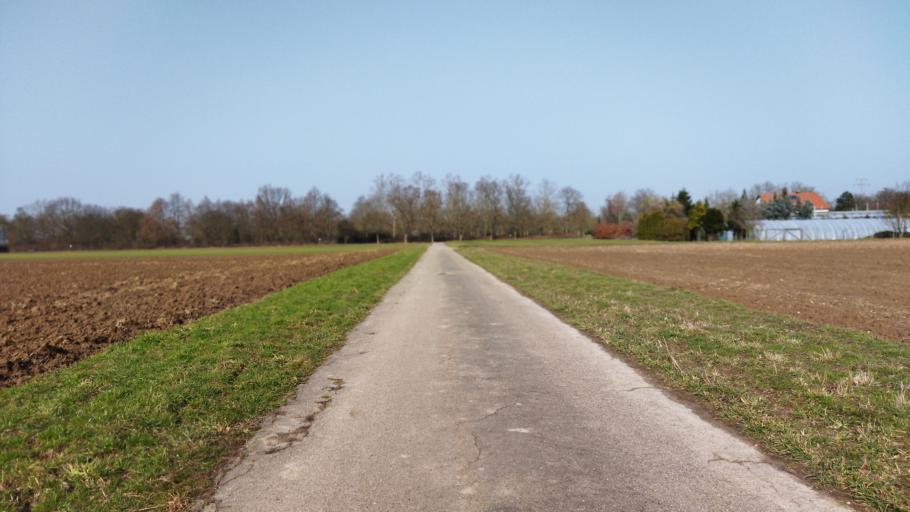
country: DE
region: Baden-Wuerttemberg
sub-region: Regierungsbezirk Stuttgart
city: Nordheim
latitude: 49.1259
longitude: 9.1654
